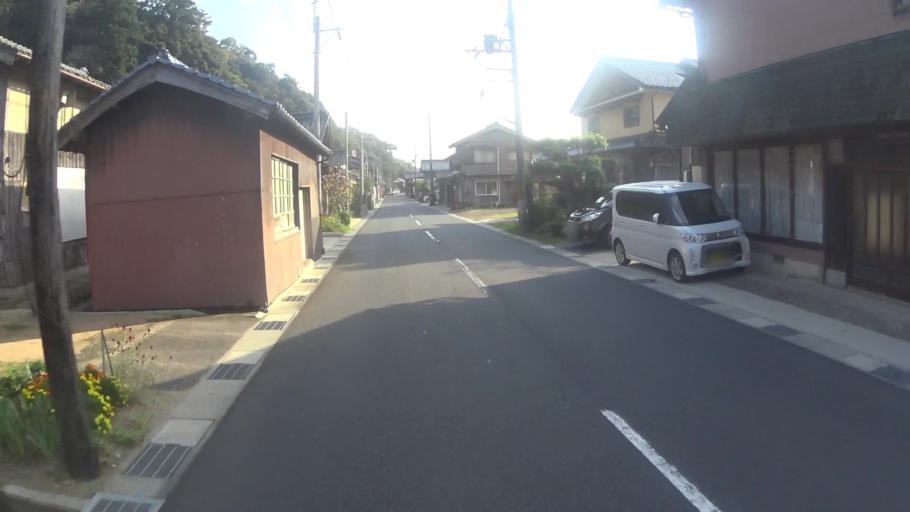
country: JP
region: Kyoto
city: Miyazu
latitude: 35.7070
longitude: 135.1055
